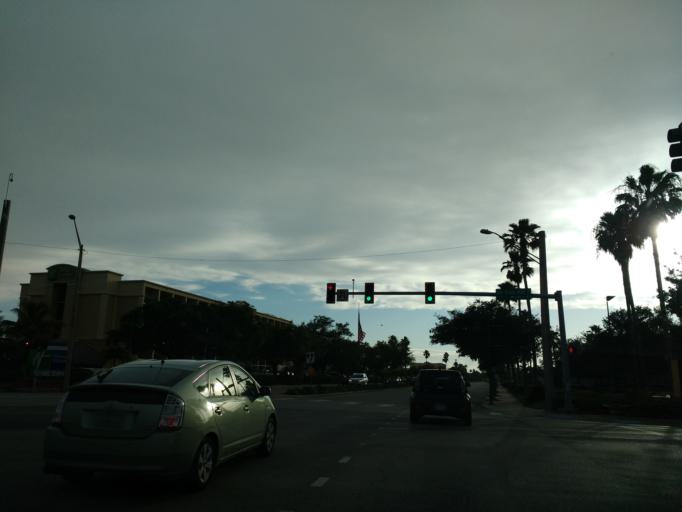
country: US
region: Florida
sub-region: Lee County
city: Cape Coral
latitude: 26.5627
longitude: -81.9438
